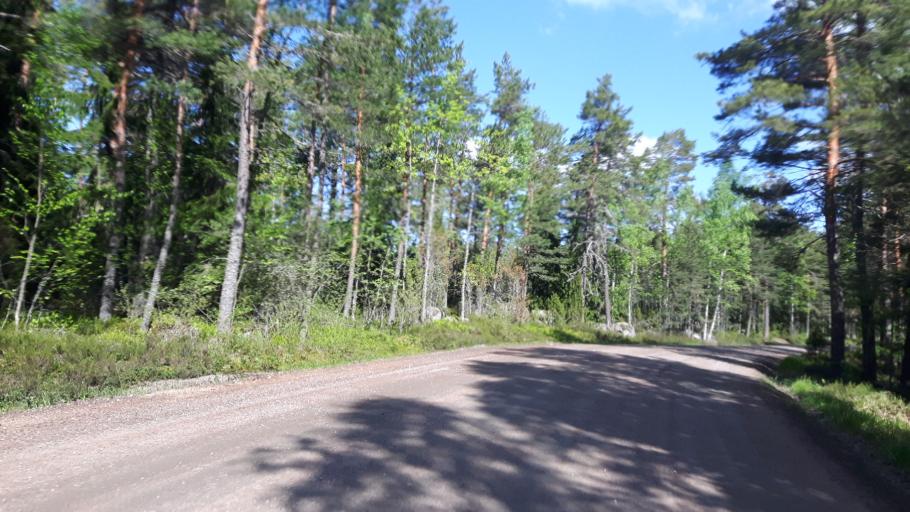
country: FI
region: Kymenlaakso
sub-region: Kotka-Hamina
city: Hamina
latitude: 60.5297
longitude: 27.2855
